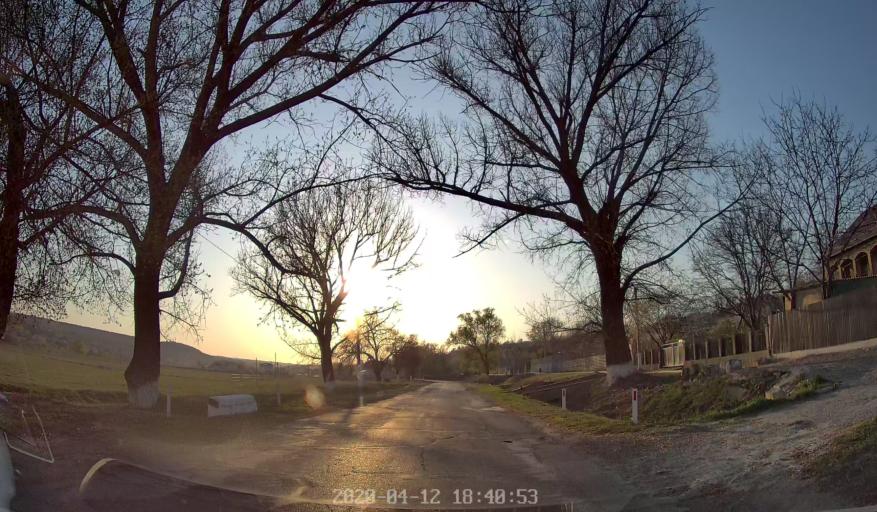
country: MD
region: Chisinau
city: Ciorescu
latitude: 47.1355
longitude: 28.9607
